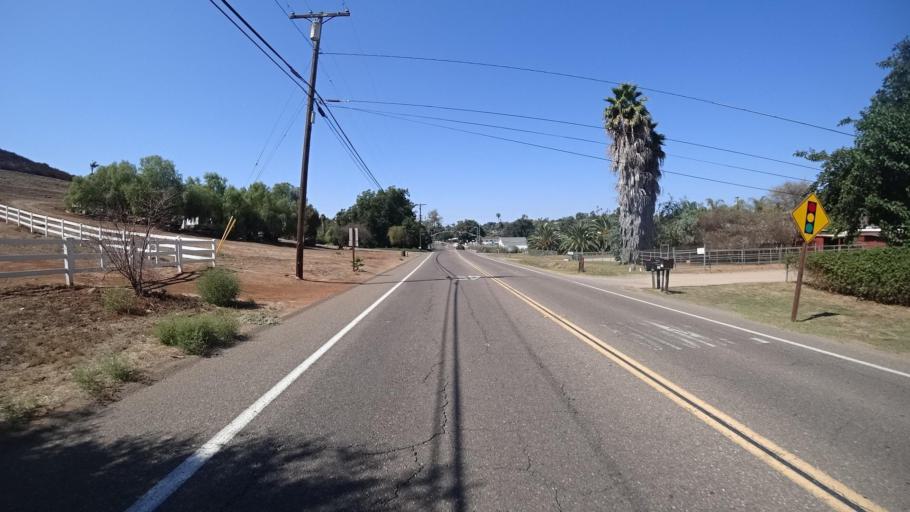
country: US
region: California
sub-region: San Diego County
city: Granite Hills
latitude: 32.8061
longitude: -116.9096
